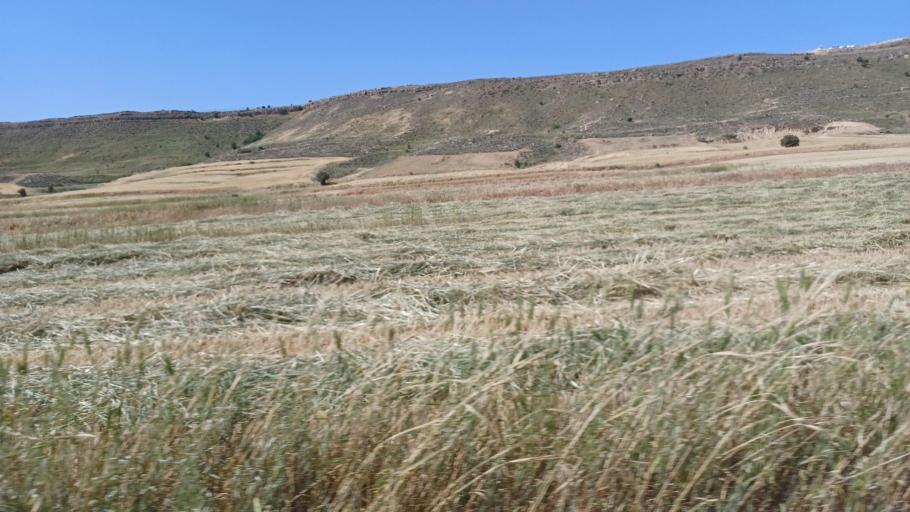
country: CY
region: Lefkosia
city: Mammari
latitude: 35.1741
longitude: 33.2204
